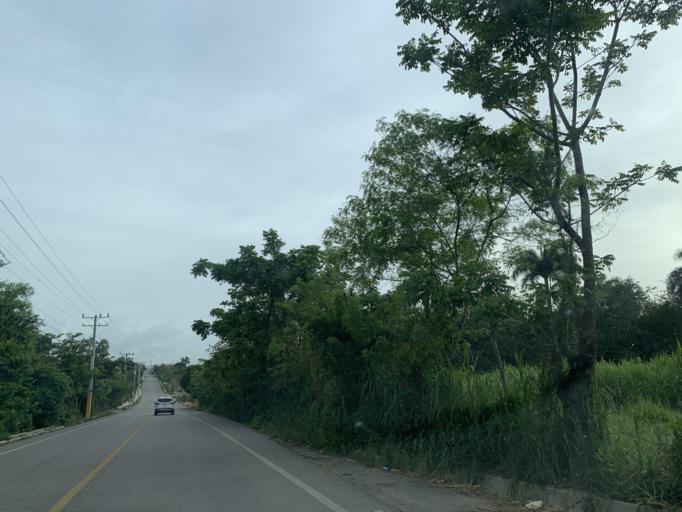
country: DO
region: Puerto Plata
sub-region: Puerto Plata
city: Puerto Plata
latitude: 19.7179
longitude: -70.6198
